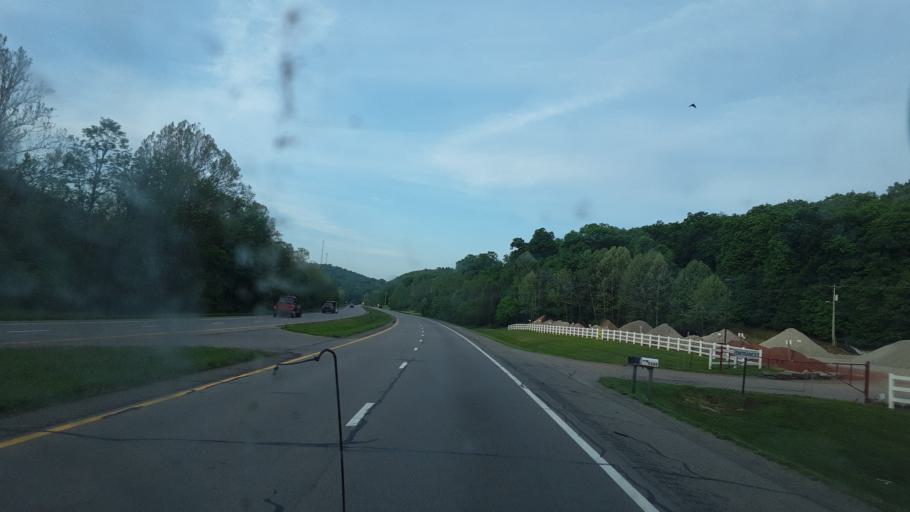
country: US
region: Ohio
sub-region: Ross County
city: Chillicothe
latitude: 39.2561
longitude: -82.9772
